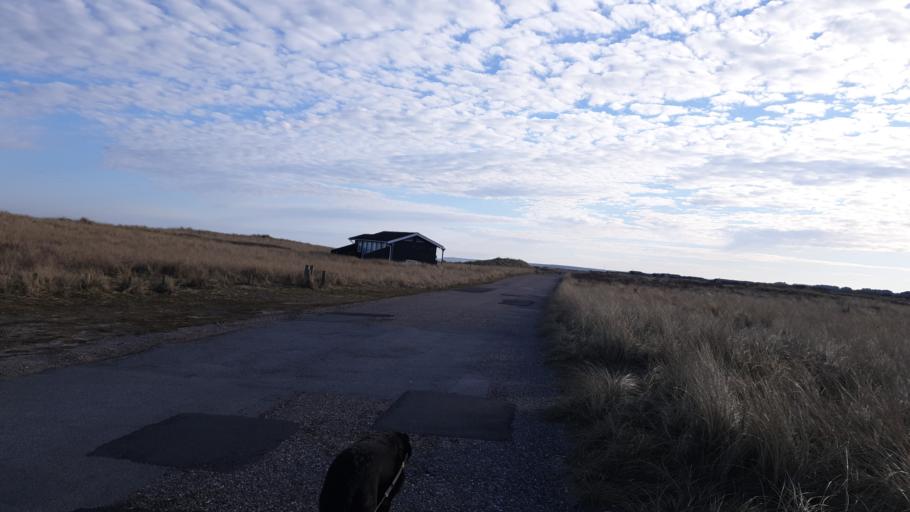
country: DK
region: North Denmark
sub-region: Hjorring Kommune
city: Hjorring
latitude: 57.4915
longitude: 9.8249
